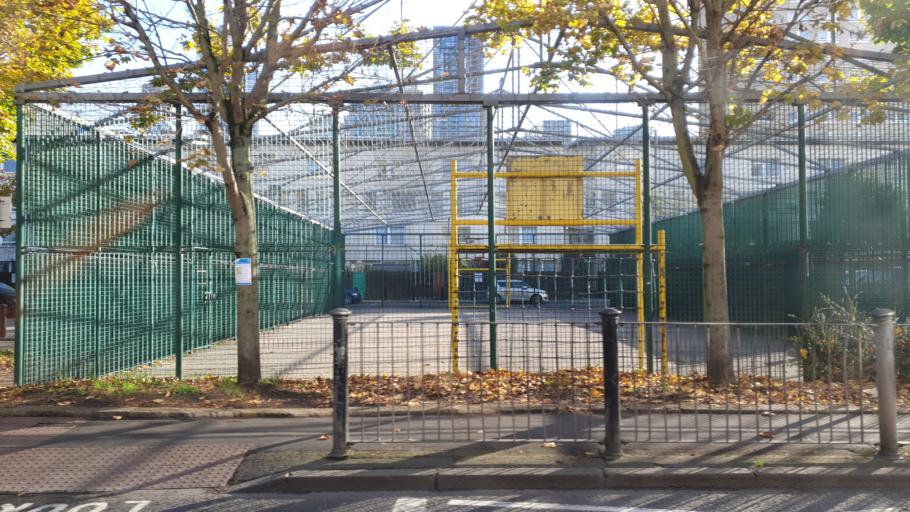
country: GB
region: England
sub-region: Greater London
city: Poplar
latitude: 51.4990
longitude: -0.0257
